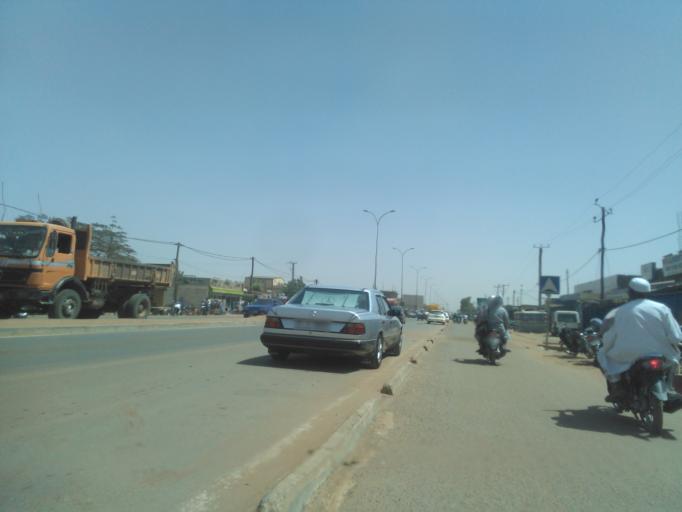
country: BF
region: Centre
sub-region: Kadiogo Province
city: Ouagadougou
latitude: 12.3345
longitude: -1.5341
